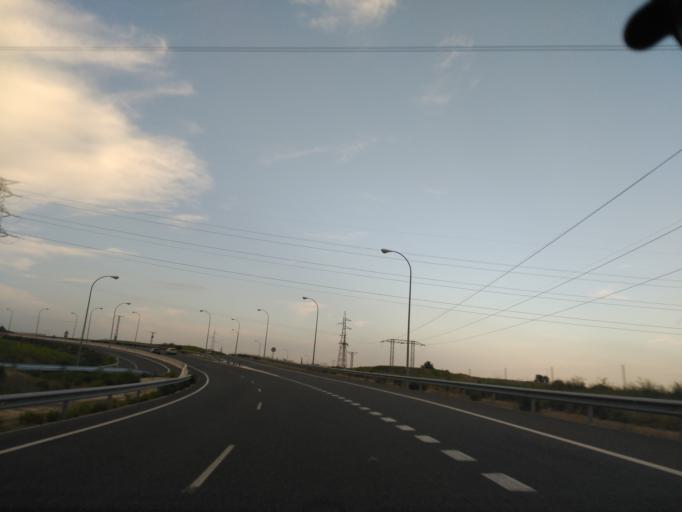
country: ES
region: Madrid
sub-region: Provincia de Madrid
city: Villaverde
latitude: 40.3324
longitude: -3.6728
